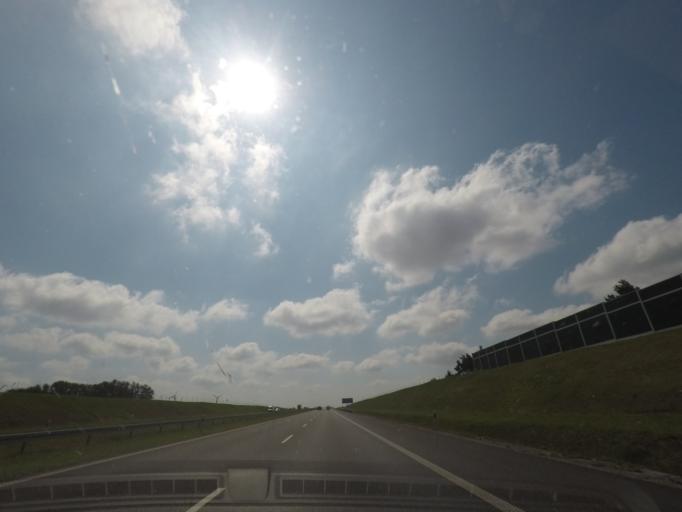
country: PL
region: Kujawsko-Pomorskie
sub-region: Powiat wloclawski
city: Brzesc Kujawski
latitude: 52.6465
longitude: 18.9422
